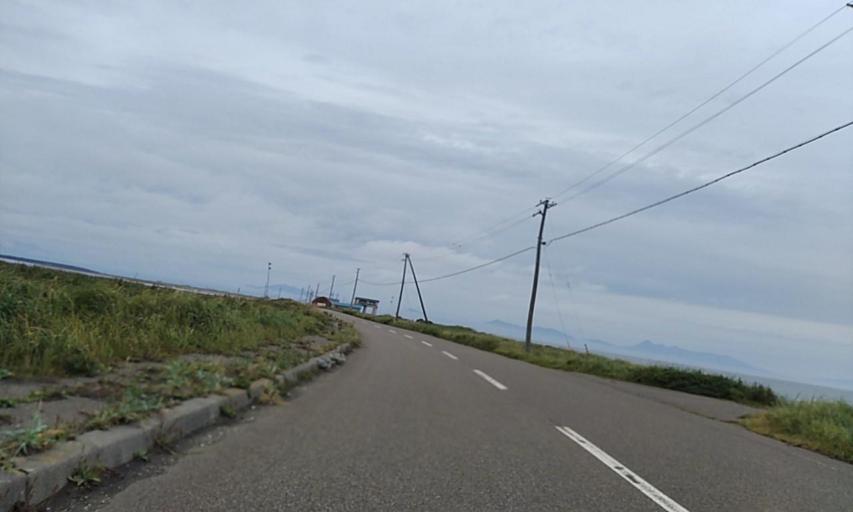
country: JP
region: Hokkaido
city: Shibetsu
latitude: 43.5869
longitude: 145.3395
